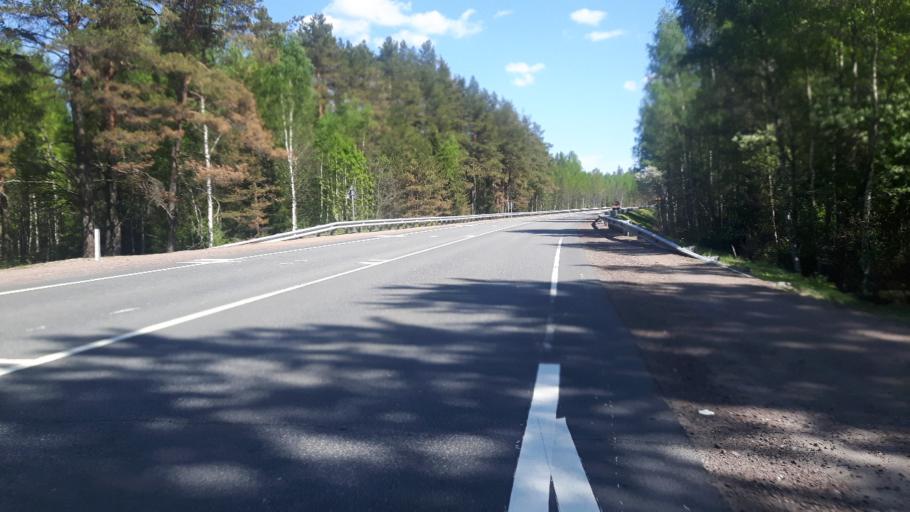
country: RU
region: Leningrad
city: Vysotsk
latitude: 60.6374
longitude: 28.2845
